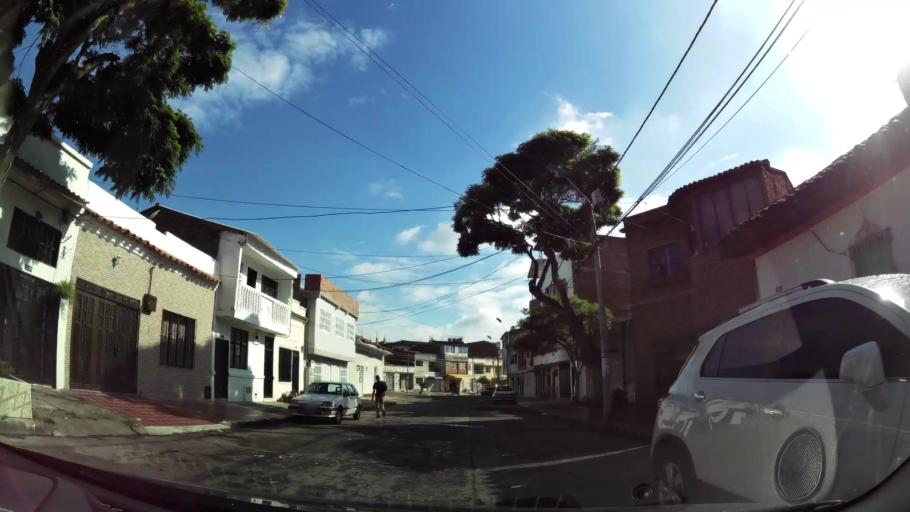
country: CO
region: Valle del Cauca
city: Cali
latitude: 3.4390
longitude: -76.5353
